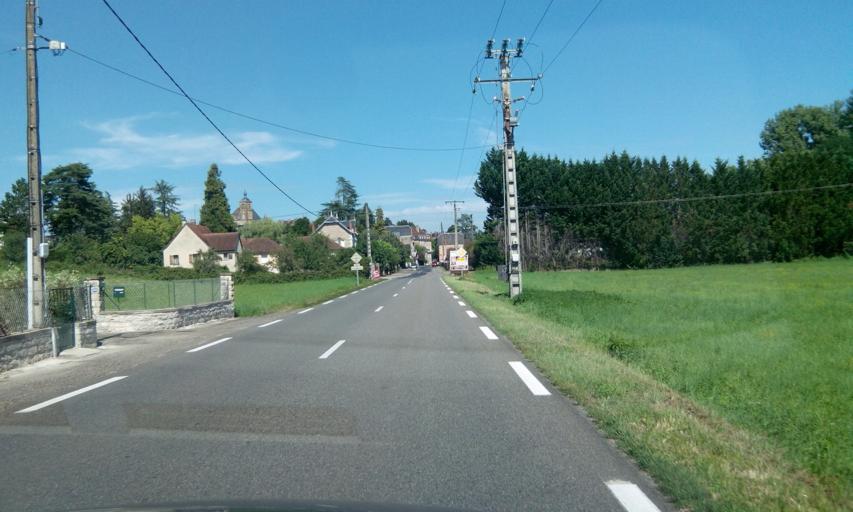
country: FR
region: Midi-Pyrenees
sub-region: Departement du Lot
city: Vayrac
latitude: 44.9501
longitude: 1.6986
